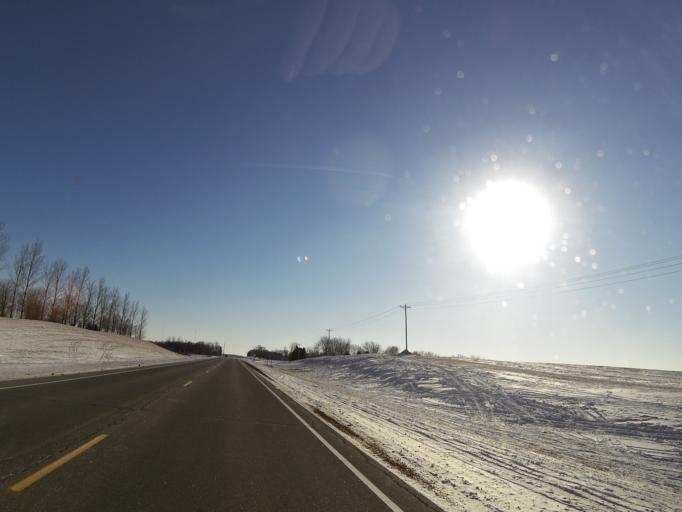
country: US
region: Minnesota
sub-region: Le Sueur County
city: New Prague
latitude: 44.5868
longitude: -93.5068
